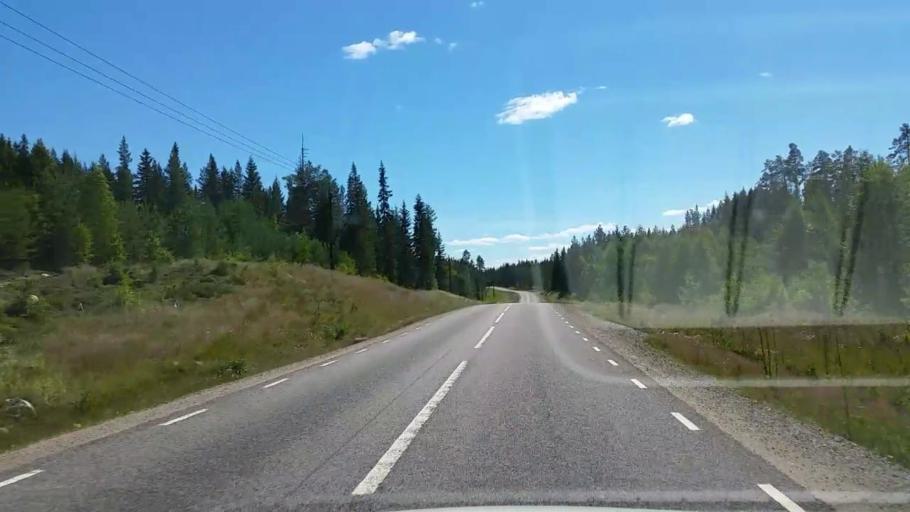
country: SE
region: Gaevleborg
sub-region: Ovanakers Kommun
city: Edsbyn
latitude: 61.5099
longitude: 15.6827
